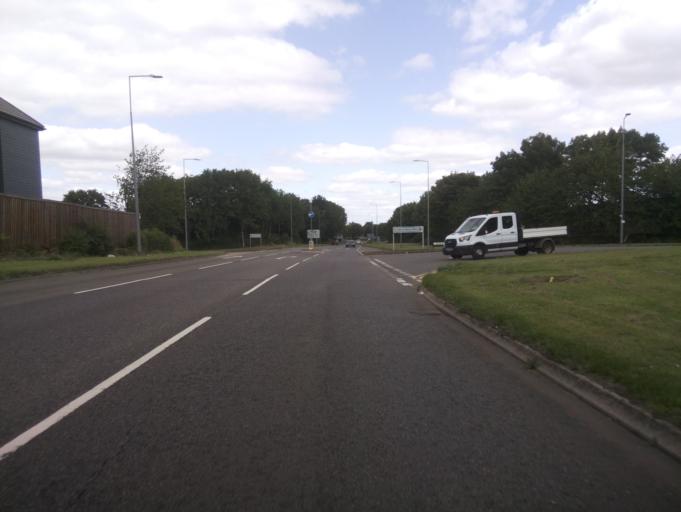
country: GB
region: England
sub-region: Milton Keynes
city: Bradwell
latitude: 52.0548
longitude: -0.7713
